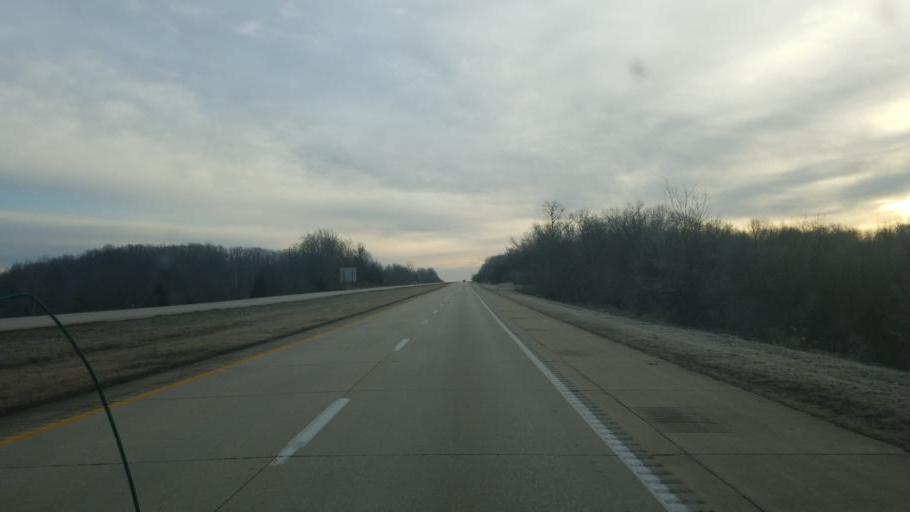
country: US
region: Missouri
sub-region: Butler County
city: Poplar Bluff
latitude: 36.7954
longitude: -90.4220
